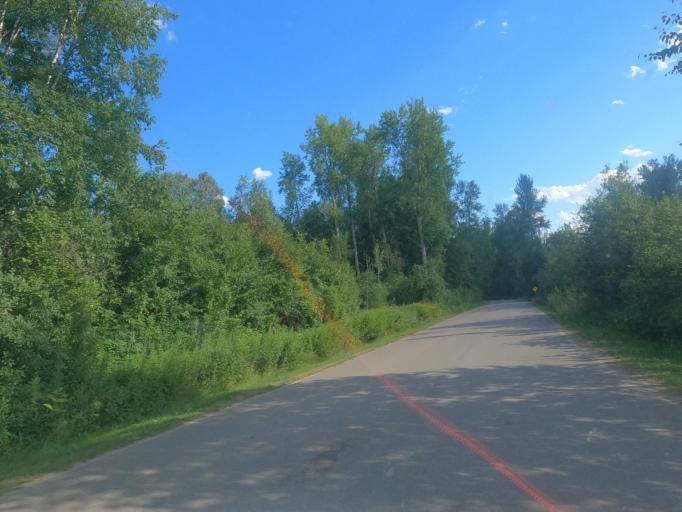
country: CA
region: British Columbia
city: Salmon Arm
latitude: 50.7333
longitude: -119.3145
